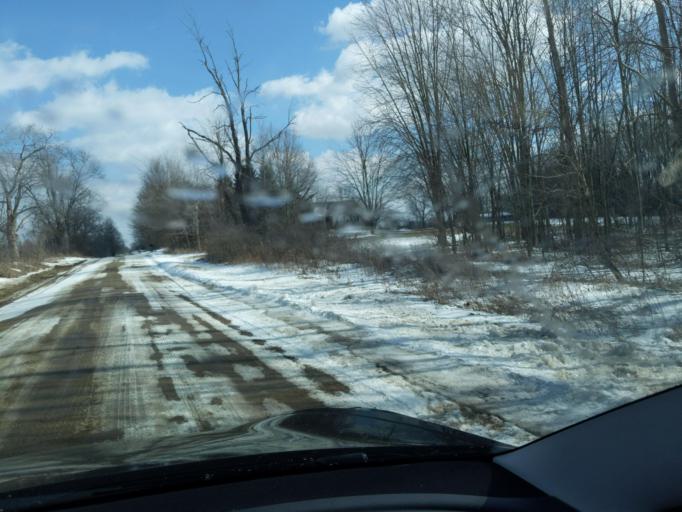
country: US
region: Michigan
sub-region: Livingston County
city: Fowlerville
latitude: 42.6139
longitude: -84.1102
